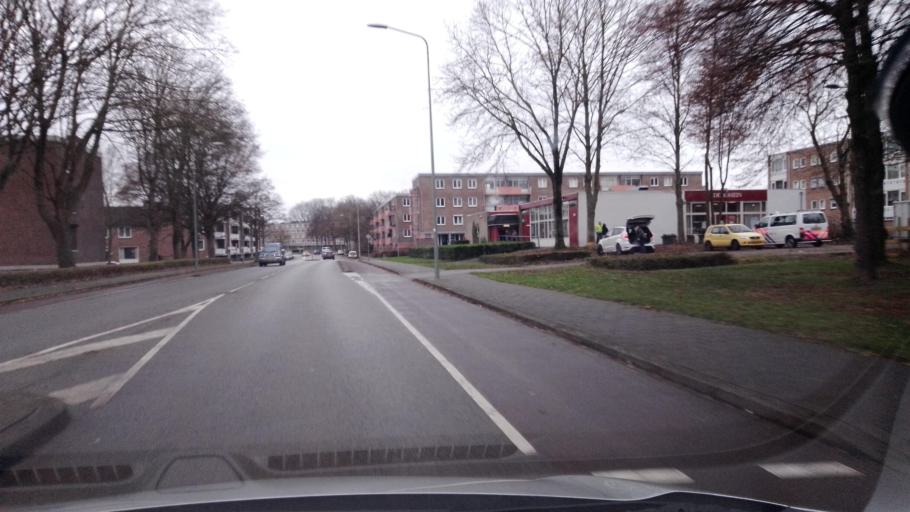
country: NL
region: Limburg
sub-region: Gemeente Maastricht
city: Maastricht
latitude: 50.8542
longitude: 5.6594
